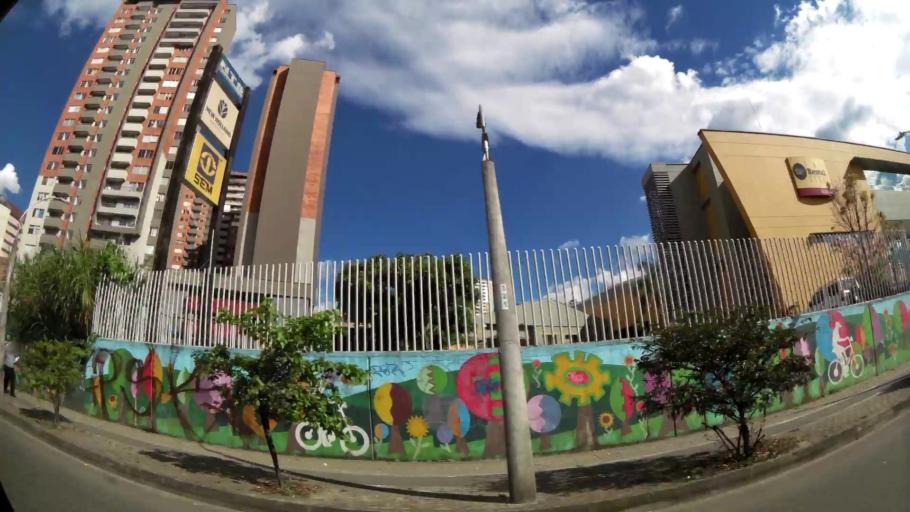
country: CO
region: Antioquia
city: Sabaneta
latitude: 6.1595
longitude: -75.6066
